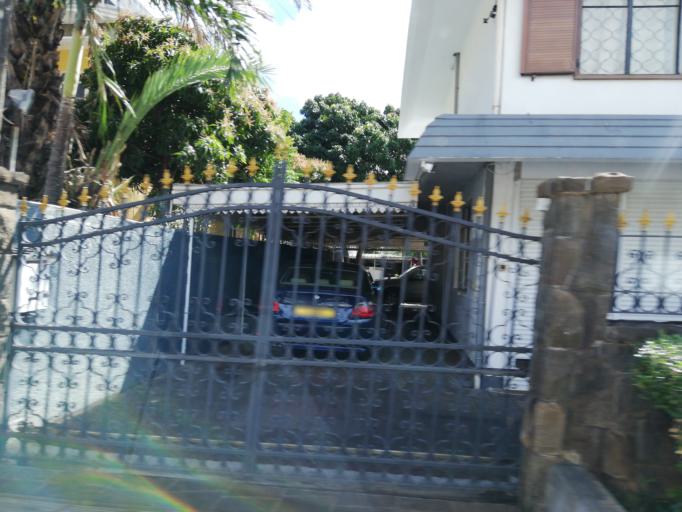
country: MU
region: Moka
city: Pailles
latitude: -20.1961
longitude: 57.4674
